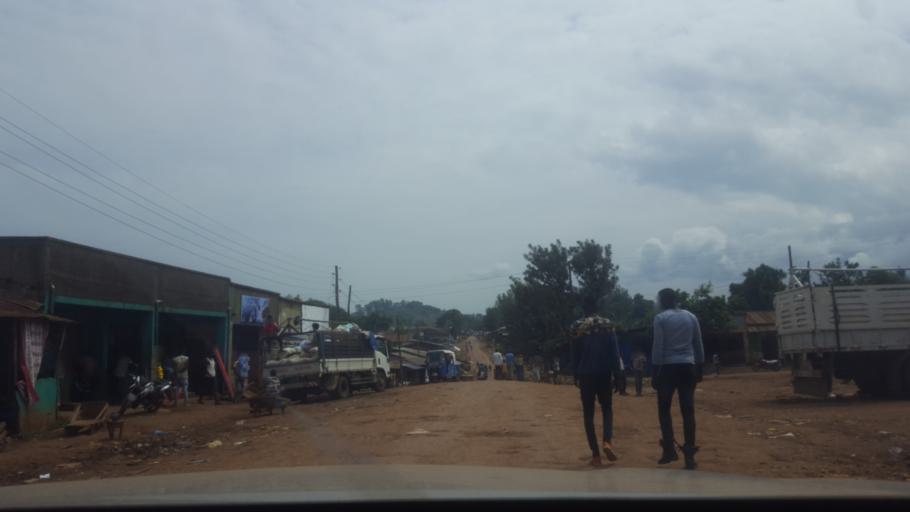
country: ET
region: Southern Nations, Nationalities, and People's Region
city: Tippi
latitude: 7.2341
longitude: 35.3185
